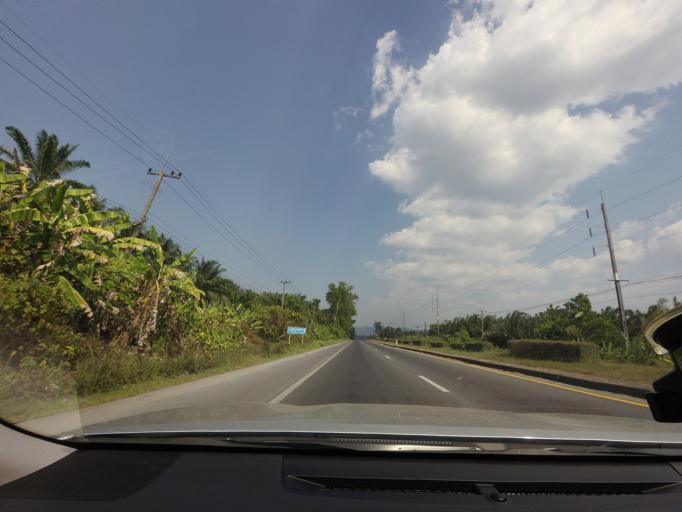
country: TH
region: Phangnga
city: Thap Put
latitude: 8.5079
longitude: 98.6694
